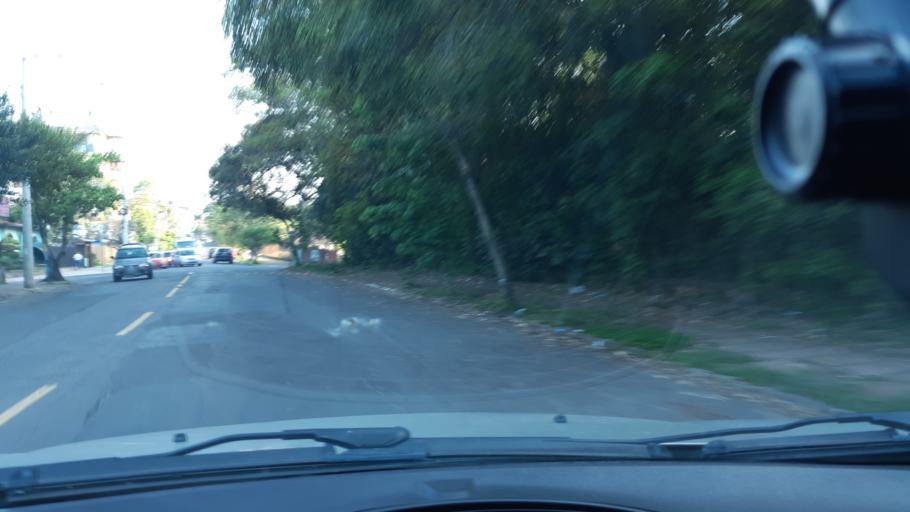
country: BR
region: Rio Grande do Sul
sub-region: Sao Leopoldo
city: Sao Leopoldo
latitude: -29.7708
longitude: -51.1362
